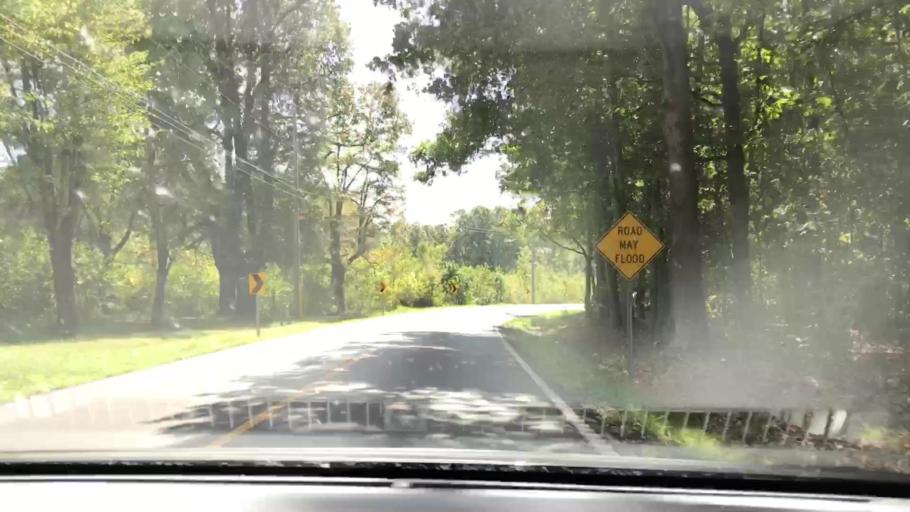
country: US
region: Kentucky
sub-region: McCracken County
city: Reidland
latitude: 36.9640
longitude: -88.5136
